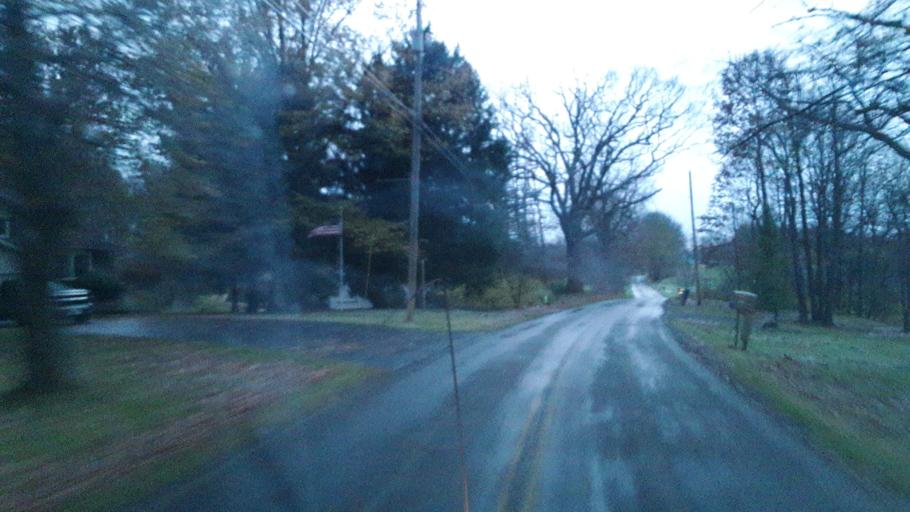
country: US
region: Ohio
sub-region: Portage County
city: Mantua
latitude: 41.3149
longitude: -81.2415
